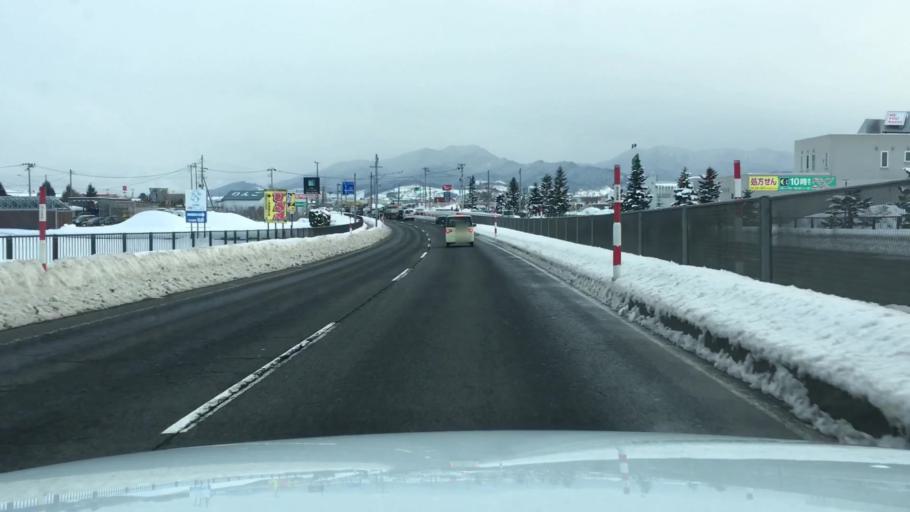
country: JP
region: Aomori
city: Hirosaki
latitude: 40.5875
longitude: 140.5069
